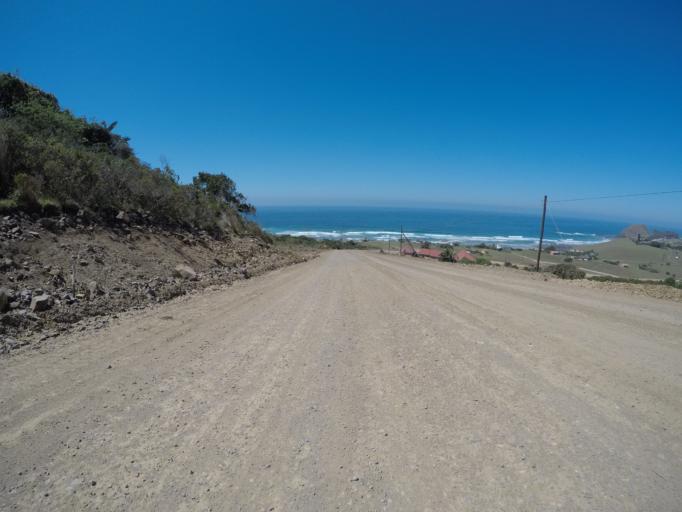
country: ZA
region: Eastern Cape
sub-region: OR Tambo District Municipality
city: Libode
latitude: -32.0254
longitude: 29.1154
